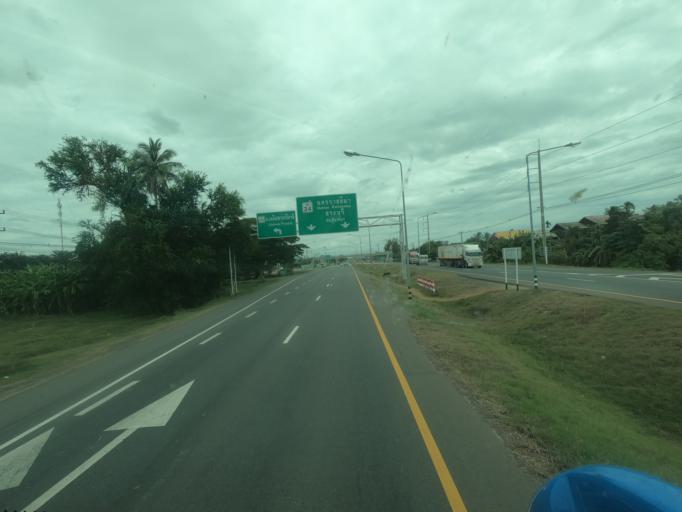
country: TH
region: Buriram
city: Chaloem Phra Kiat
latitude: 14.6097
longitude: 102.9195
